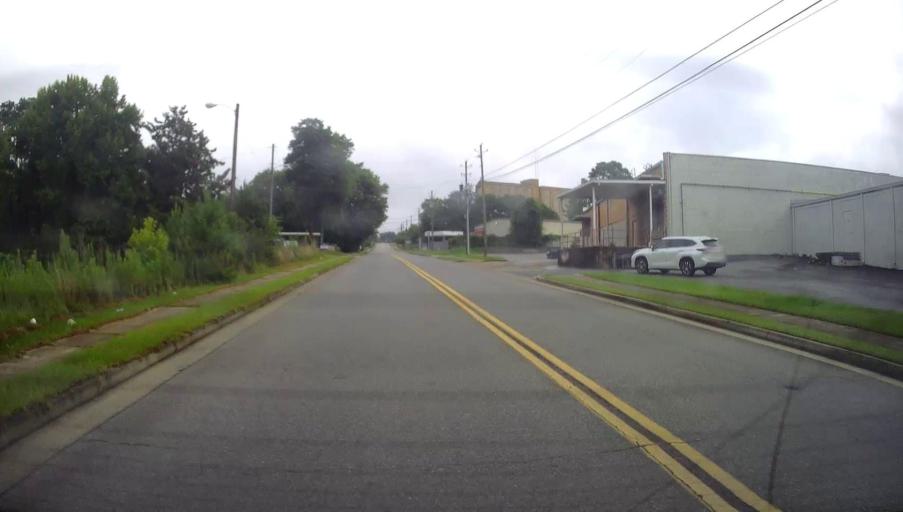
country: US
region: Georgia
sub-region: Bibb County
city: Macon
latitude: 32.8546
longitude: -83.6198
